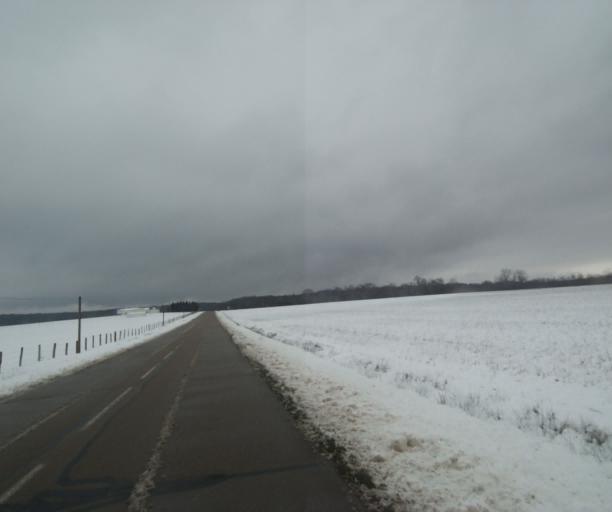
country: FR
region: Champagne-Ardenne
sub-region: Departement de la Haute-Marne
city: Laneuville-a-Remy
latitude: 48.4314
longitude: 4.8538
